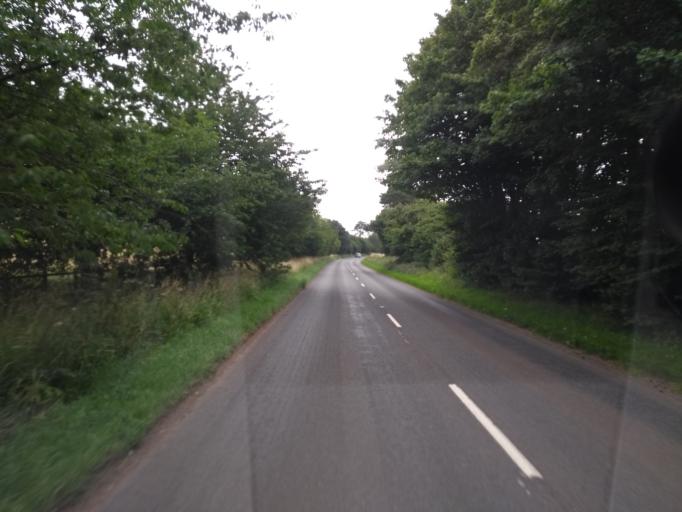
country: GB
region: England
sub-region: Somerset
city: Wiveliscombe
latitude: 51.0415
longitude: -3.3009
